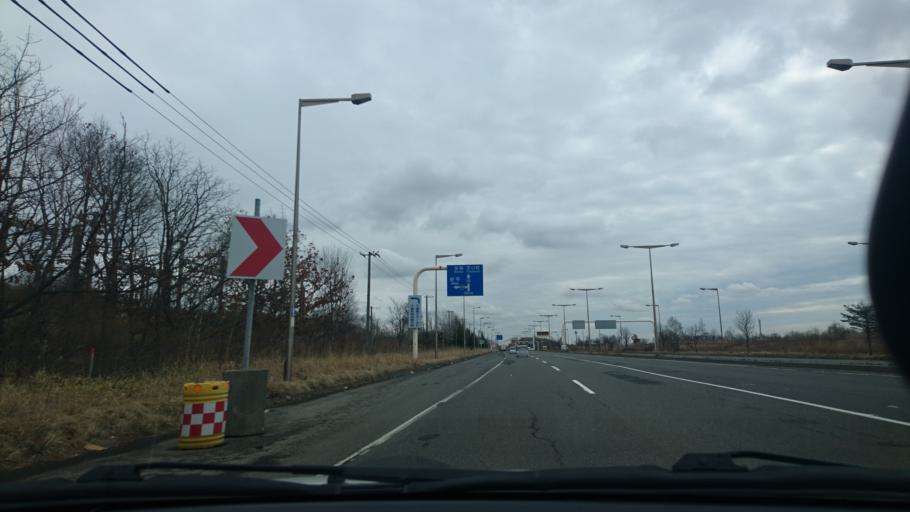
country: JP
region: Hokkaido
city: Chitose
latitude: 42.7985
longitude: 141.6863
